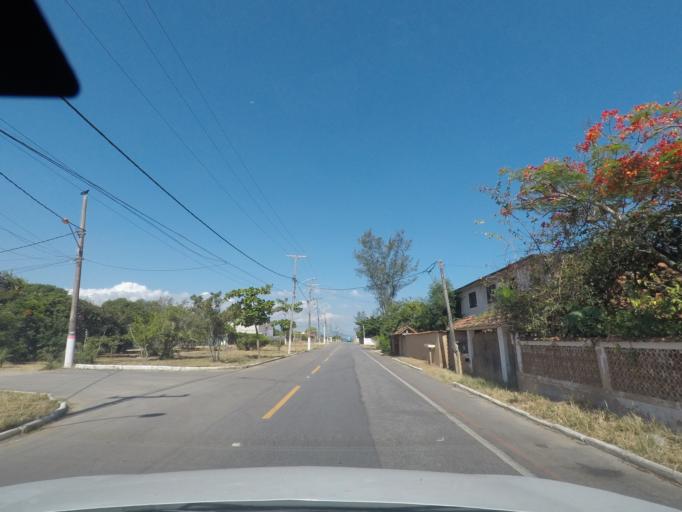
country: BR
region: Rio de Janeiro
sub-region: Marica
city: Marica
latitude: -22.9691
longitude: -42.9075
